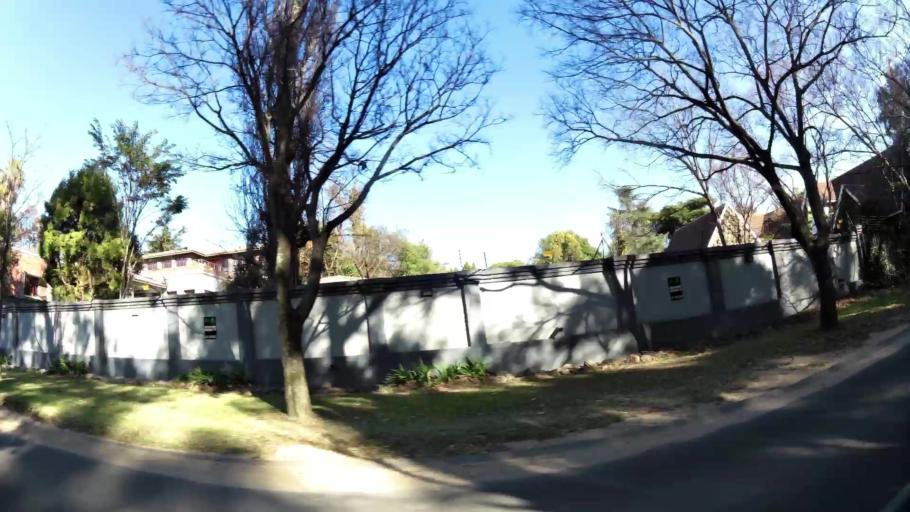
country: ZA
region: Gauteng
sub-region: City of Johannesburg Metropolitan Municipality
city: Diepsloot
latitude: -26.0483
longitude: 27.9874
